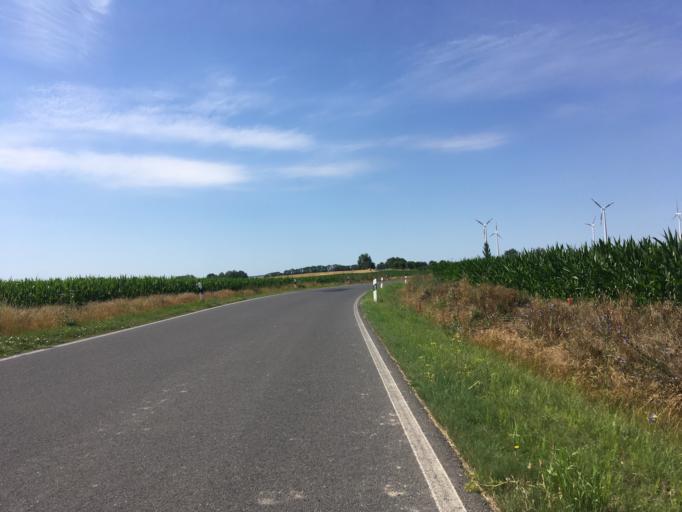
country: DE
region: Brandenburg
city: Gramzow
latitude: 53.2671
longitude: 14.0688
